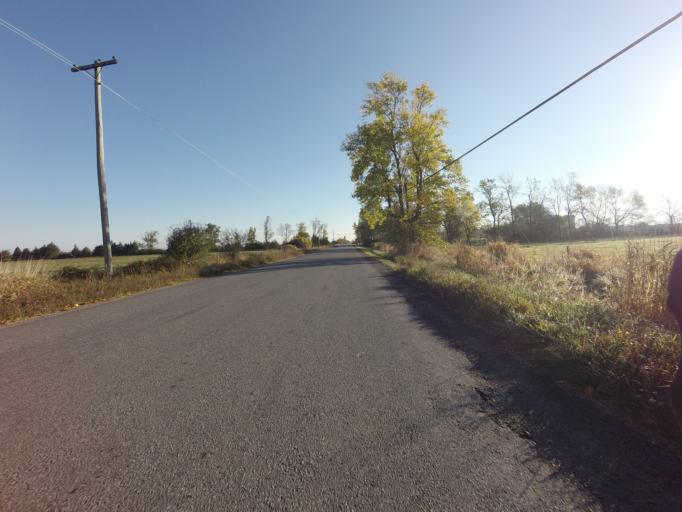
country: CA
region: Ontario
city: Belleville
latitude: 44.0515
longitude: -77.4204
